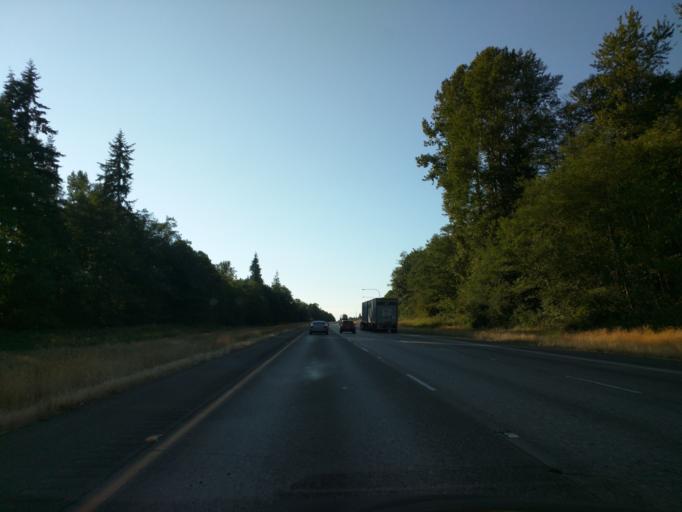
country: US
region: Washington
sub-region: Snohomish County
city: Bryant
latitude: 48.2492
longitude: -122.2507
